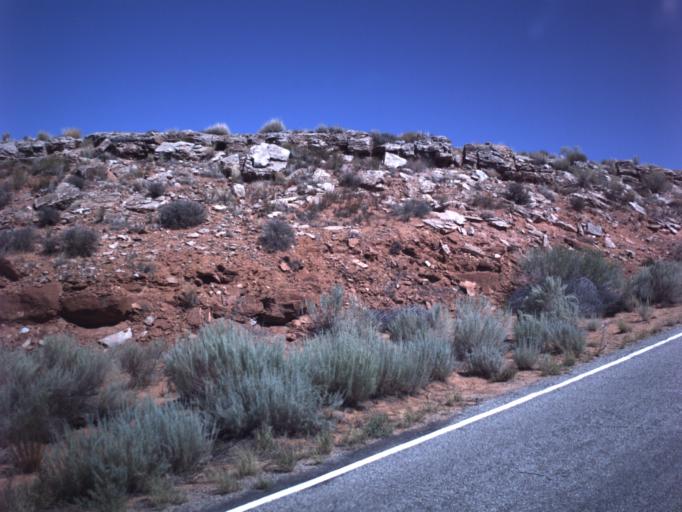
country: US
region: Utah
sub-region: San Juan County
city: Blanding
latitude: 37.1997
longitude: -109.8822
